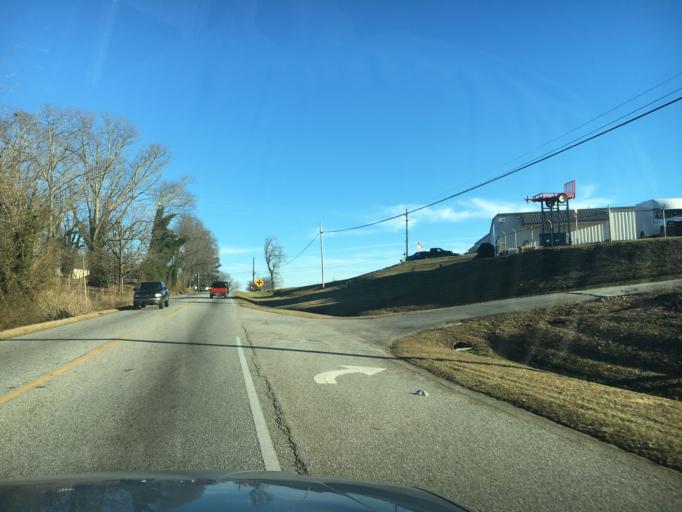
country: US
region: Georgia
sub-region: Habersham County
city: Demorest
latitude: 34.5466
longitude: -83.5504
